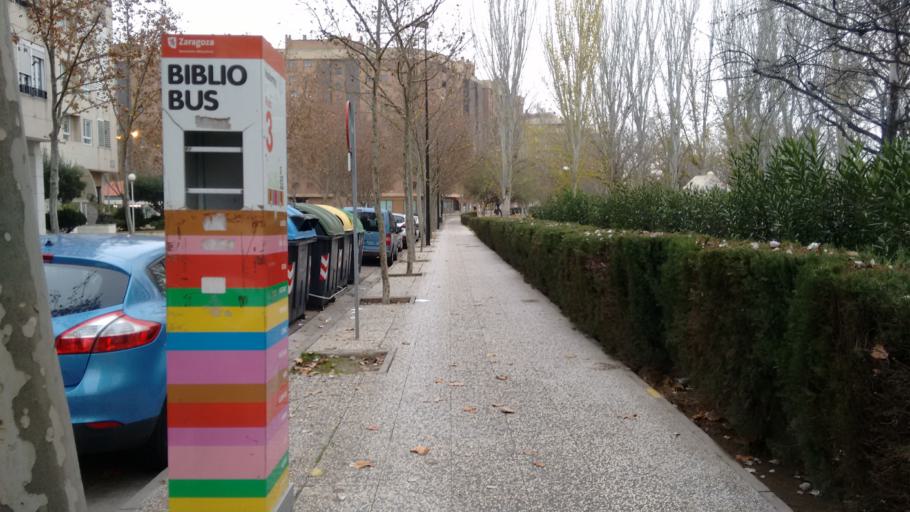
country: ES
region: Aragon
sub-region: Provincia de Zaragoza
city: Zaragoza
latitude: 41.6568
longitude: -0.8587
